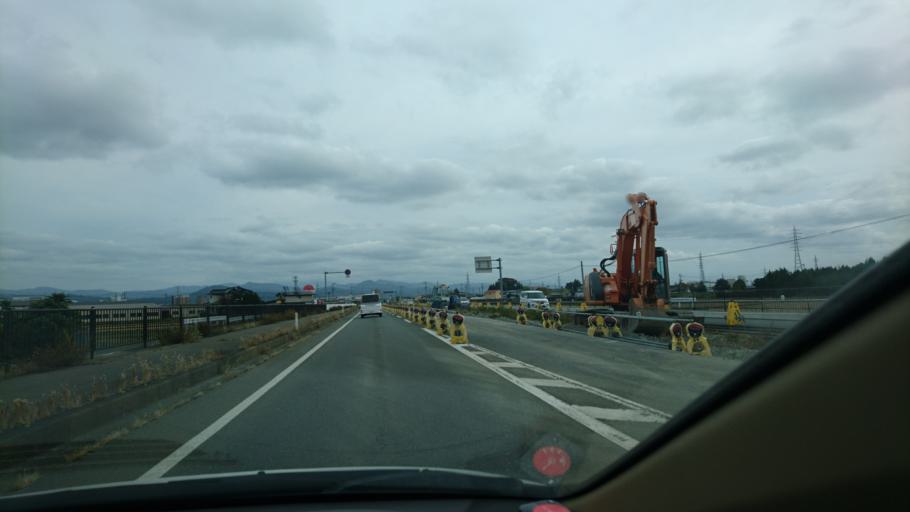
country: JP
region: Iwate
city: Morioka-shi
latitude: 39.6918
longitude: 141.1083
